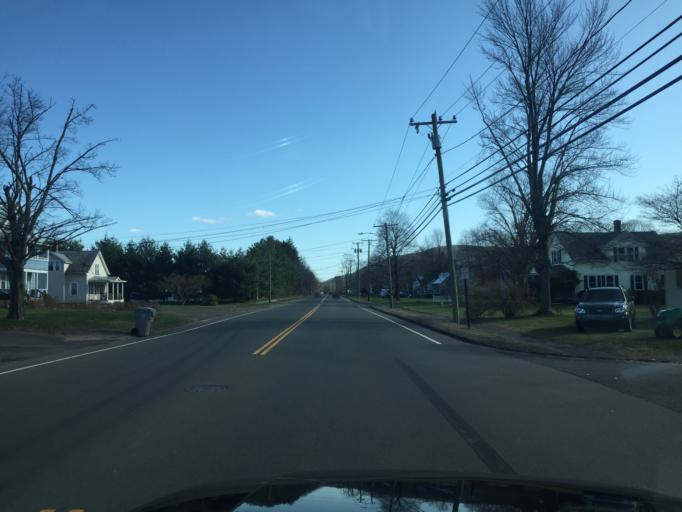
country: US
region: Connecticut
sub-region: Hartford County
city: Bristol
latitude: 41.6625
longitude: -72.9225
